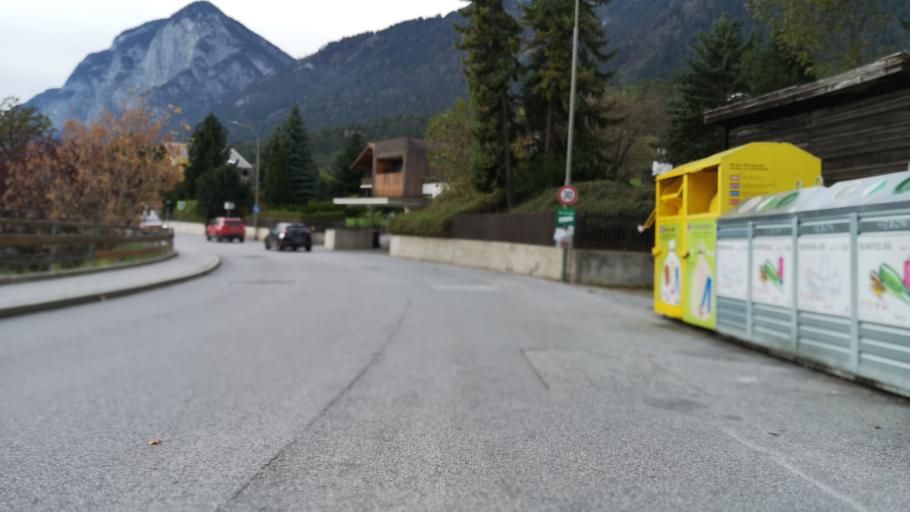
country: AT
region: Tyrol
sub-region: Innsbruck Stadt
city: Innsbruck
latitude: 47.2692
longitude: 11.3645
